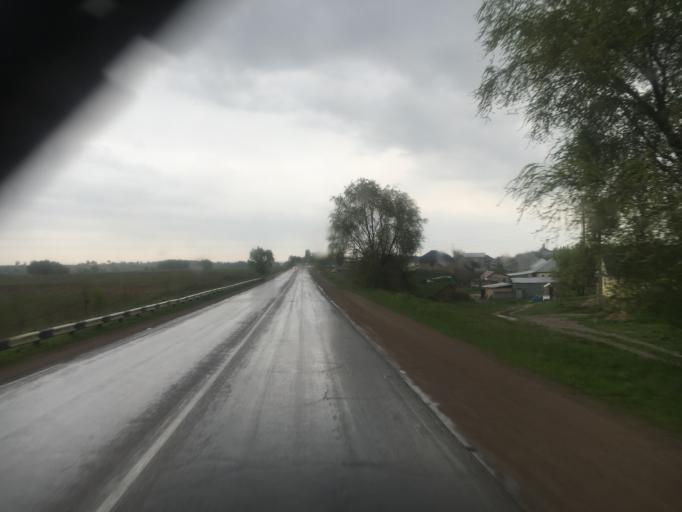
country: KZ
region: Almaty Oblysy
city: Burunday
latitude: 43.2917
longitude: 76.6732
